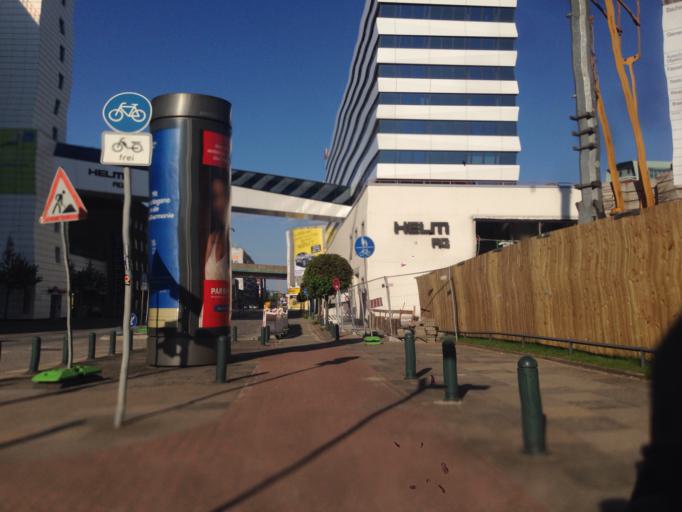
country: DE
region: Hamburg
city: Hamburg-Mitte
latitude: 53.5491
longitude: 10.0182
